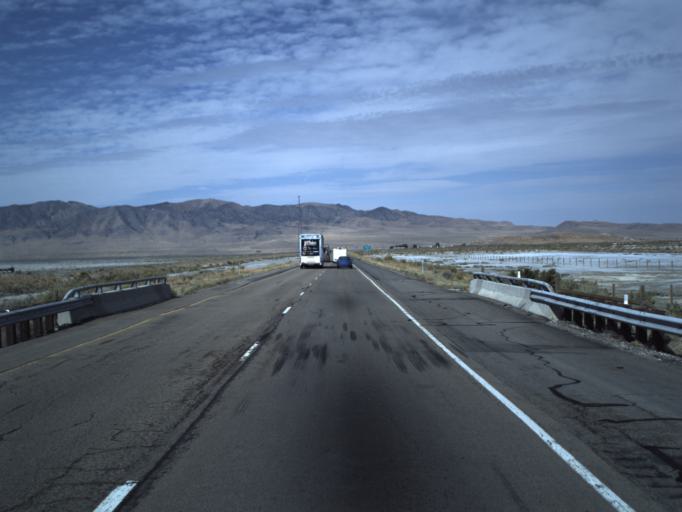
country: US
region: Utah
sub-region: Tooele County
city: Grantsville
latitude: 40.7564
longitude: -112.7553
